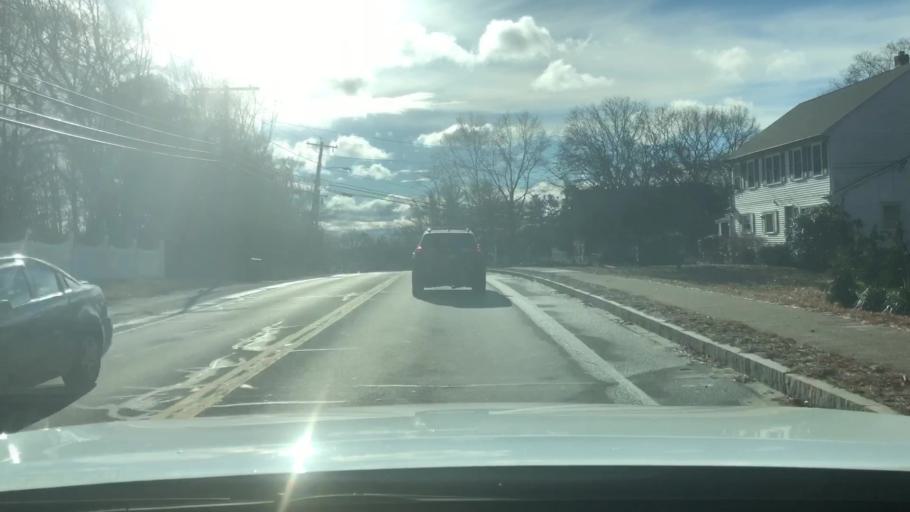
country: US
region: Massachusetts
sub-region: Norfolk County
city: Bellingham
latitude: 42.0559
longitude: -71.4850
